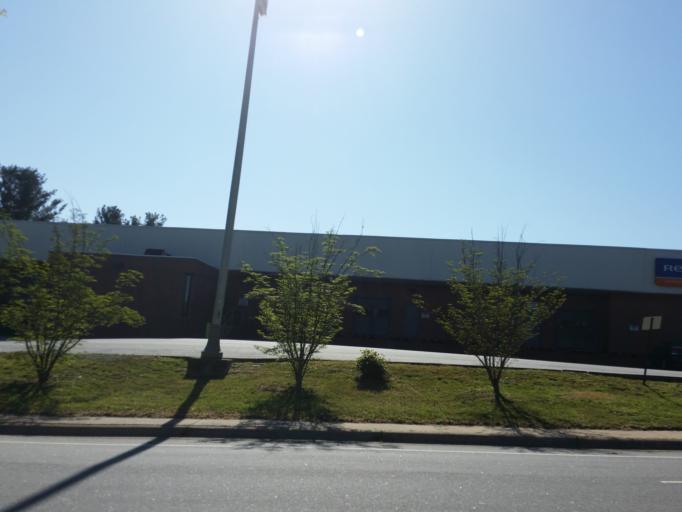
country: US
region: North Carolina
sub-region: Buncombe County
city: Asheville
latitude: 35.5879
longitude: -82.5563
